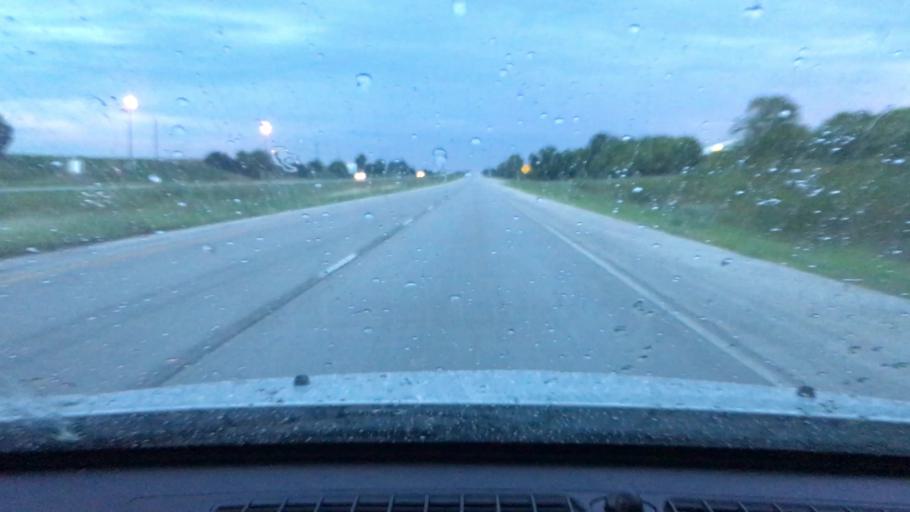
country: US
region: Illinois
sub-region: Morgan County
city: South Jacksonville
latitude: 39.7220
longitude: -90.1693
